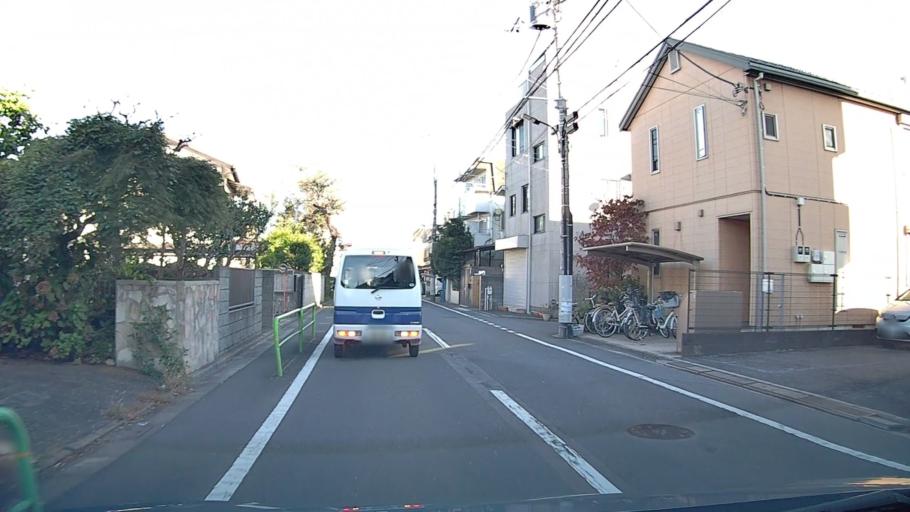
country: JP
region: Tokyo
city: Nishi-Tokyo-shi
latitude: 35.7546
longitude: 139.5768
